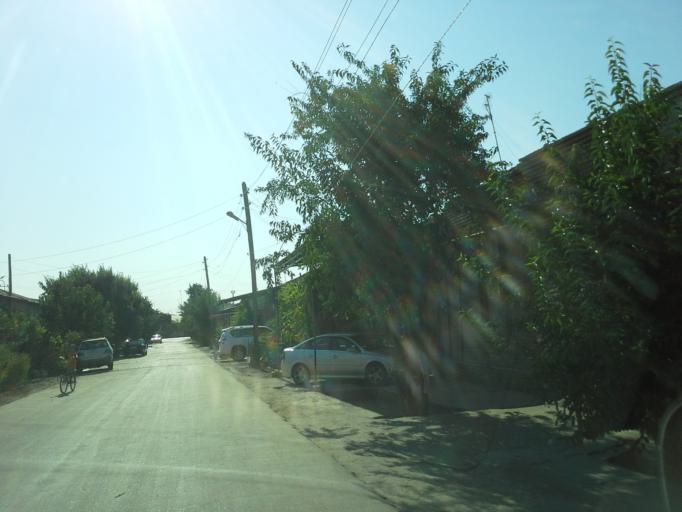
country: TM
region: Dasoguz
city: Dasoguz
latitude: 41.8257
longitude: 59.9779
